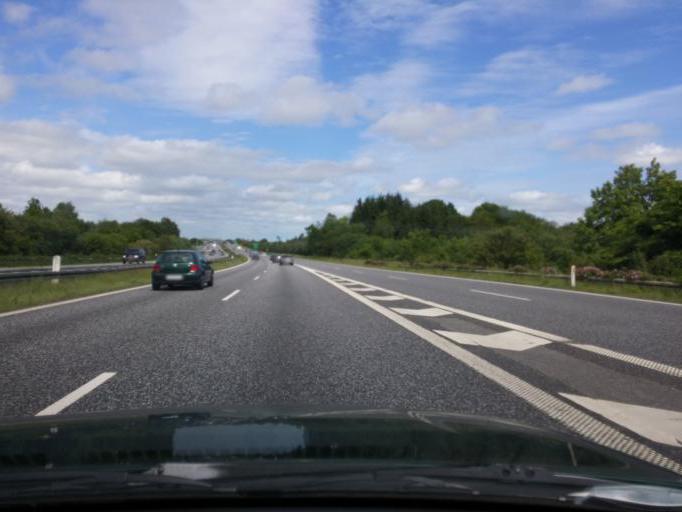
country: DK
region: South Denmark
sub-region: Kolding Kommune
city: Kolding
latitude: 55.5346
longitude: 9.5012
